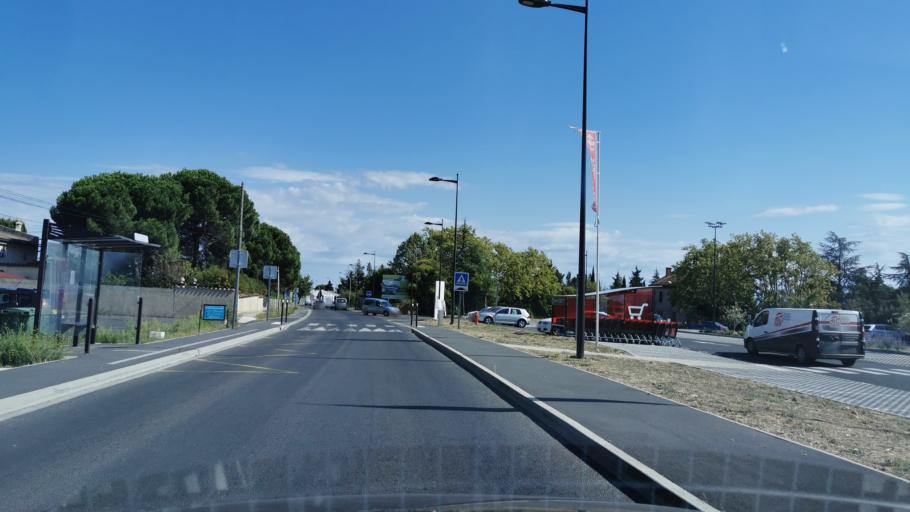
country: FR
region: Languedoc-Roussillon
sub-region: Departement de l'Aude
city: Peyriac-Minervois
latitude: 43.2856
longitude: 2.5726
